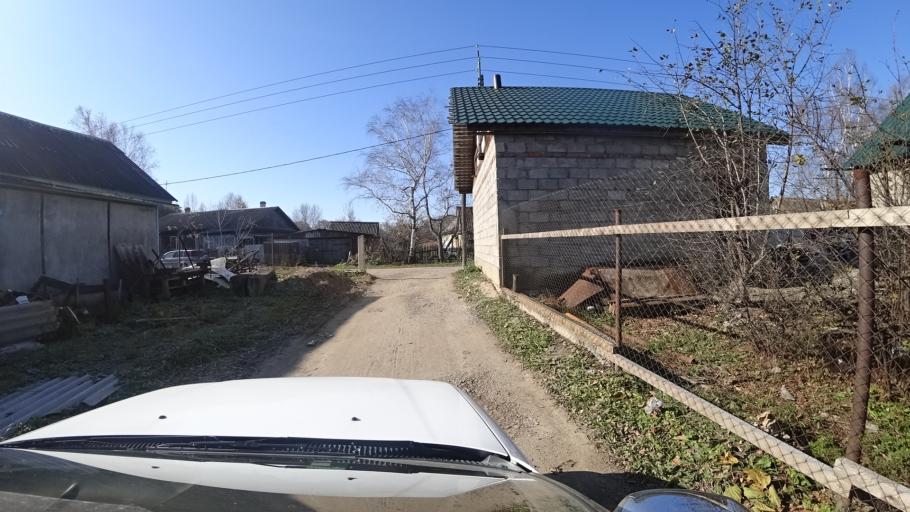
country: RU
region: Primorskiy
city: Dal'nerechensk
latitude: 45.9074
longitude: 133.8012
